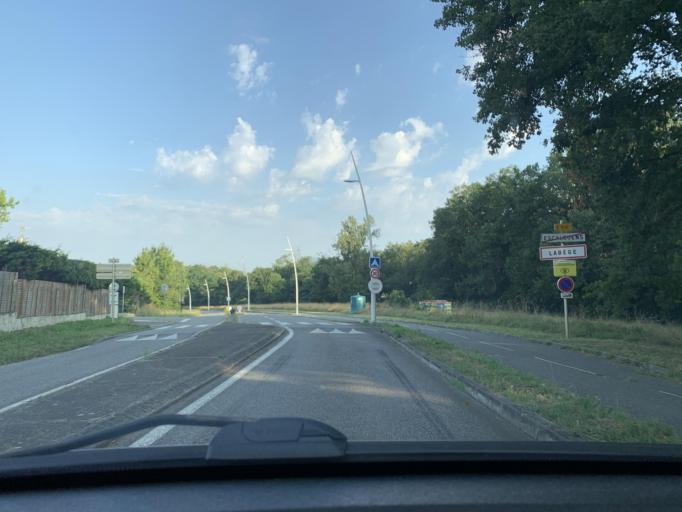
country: FR
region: Midi-Pyrenees
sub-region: Departement de la Haute-Garonne
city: Labege
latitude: 43.5335
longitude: 1.5465
